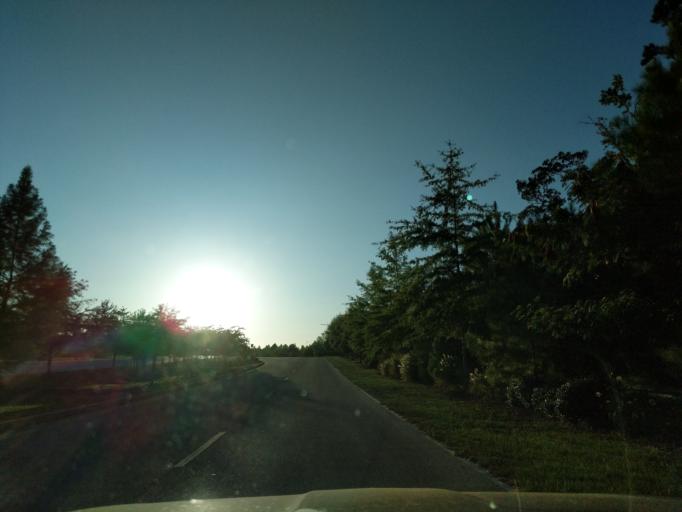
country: US
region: Georgia
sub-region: Columbia County
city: Grovetown
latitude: 33.4797
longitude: -82.1894
